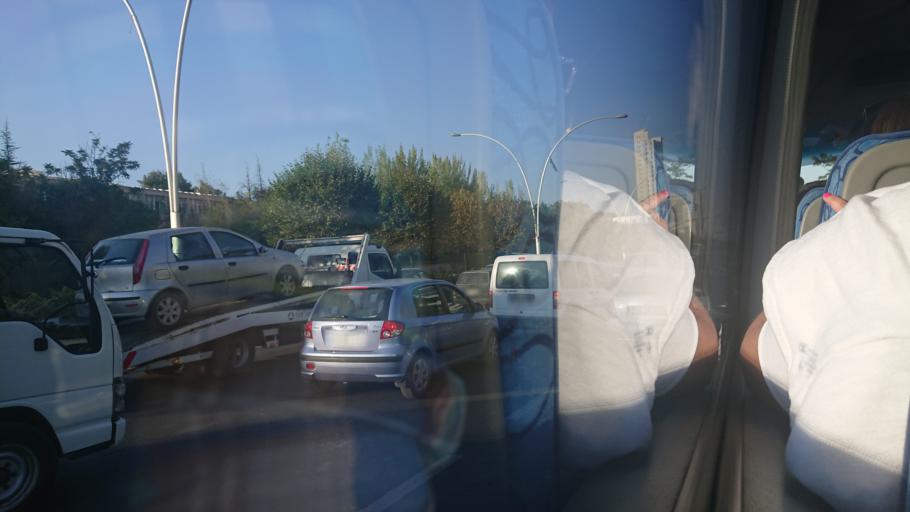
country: TR
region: Ankara
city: Ankara
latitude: 39.9339
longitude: 32.8214
